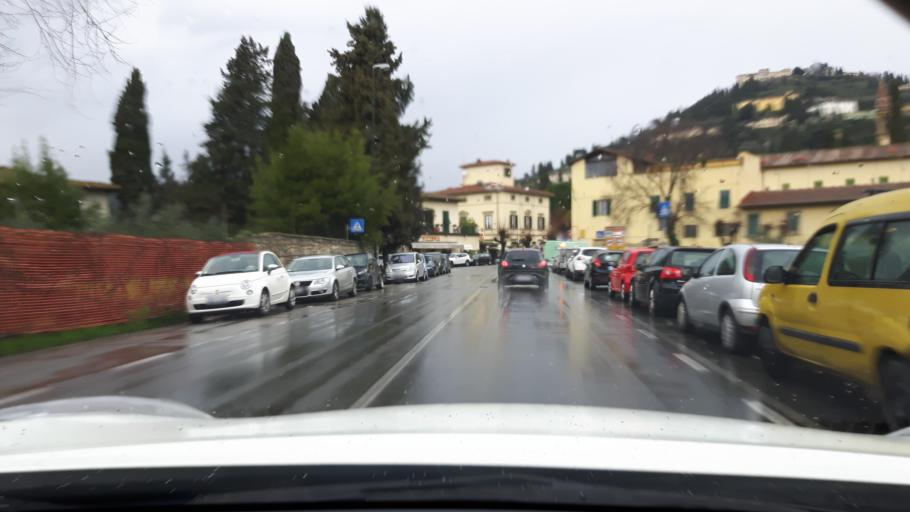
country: IT
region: Tuscany
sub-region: Province of Florence
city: Fiesole
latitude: 43.8001
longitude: 11.2852
